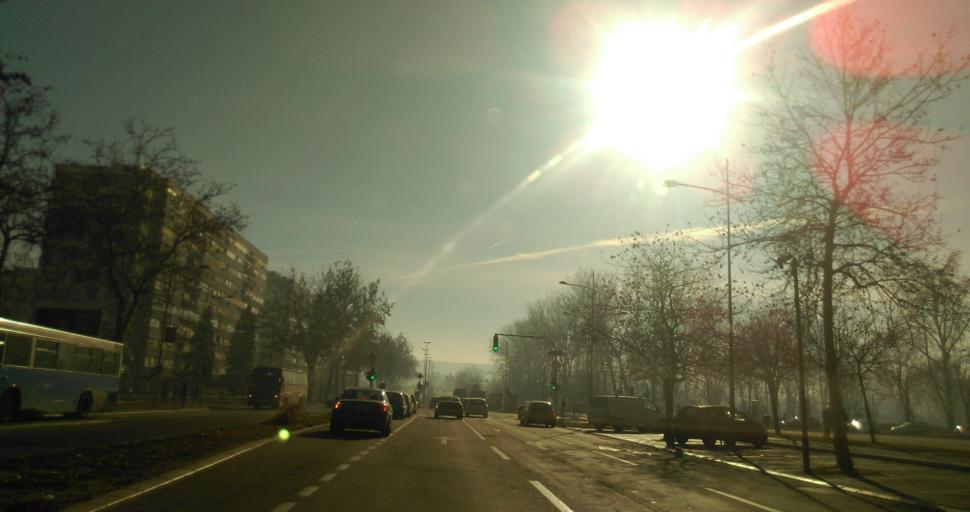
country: RS
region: Autonomna Pokrajina Vojvodina
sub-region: Juznobacki Okrug
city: Novi Sad
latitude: 45.2424
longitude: 19.8422
